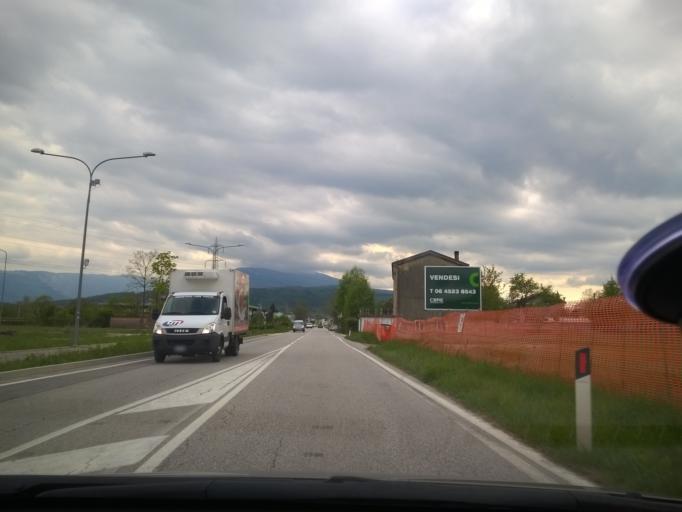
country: IT
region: Veneto
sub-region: Provincia di Belluno
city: Ponte nelle Alpi-Polpet
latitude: 46.1928
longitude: 12.2867
